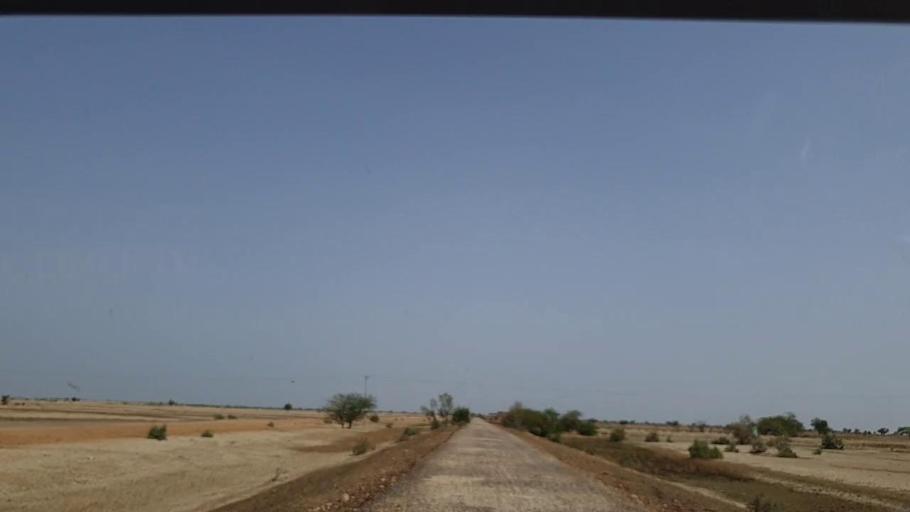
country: PK
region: Sindh
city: Johi
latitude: 26.7722
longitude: 67.6557
